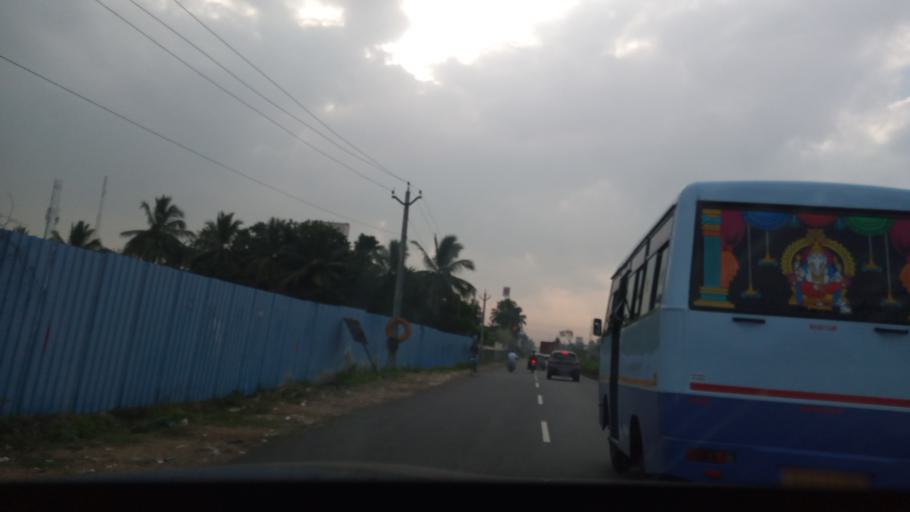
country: IN
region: Tamil Nadu
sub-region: Kancheepuram
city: Vengavasal
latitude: 12.8335
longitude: 80.1585
